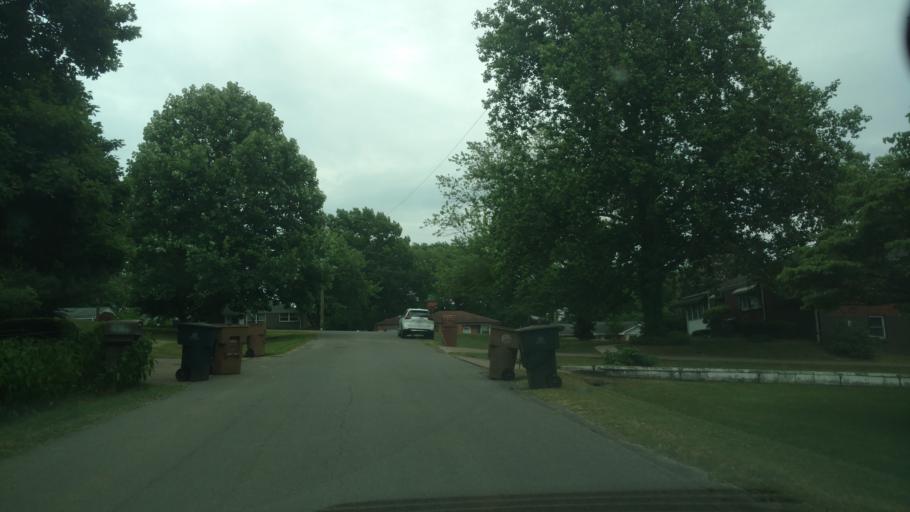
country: US
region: Tennessee
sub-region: Davidson County
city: Lakewood
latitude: 36.2020
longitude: -86.7022
